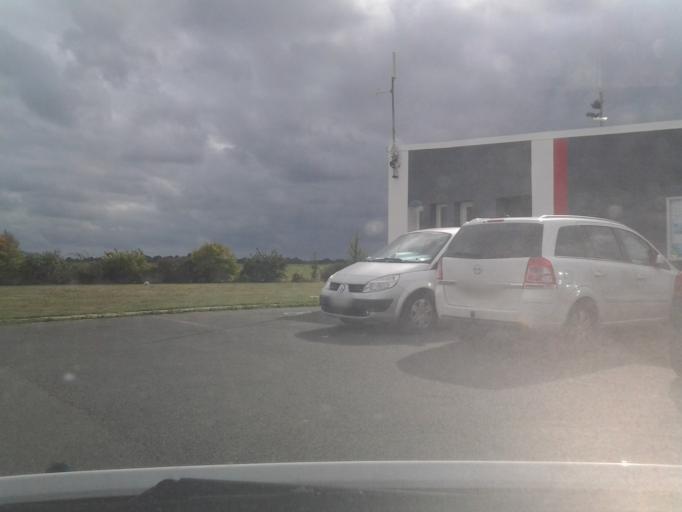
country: FR
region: Pays de la Loire
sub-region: Departement de la Vendee
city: Dompierre-sur-Yon
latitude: 46.7046
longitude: -1.3765
